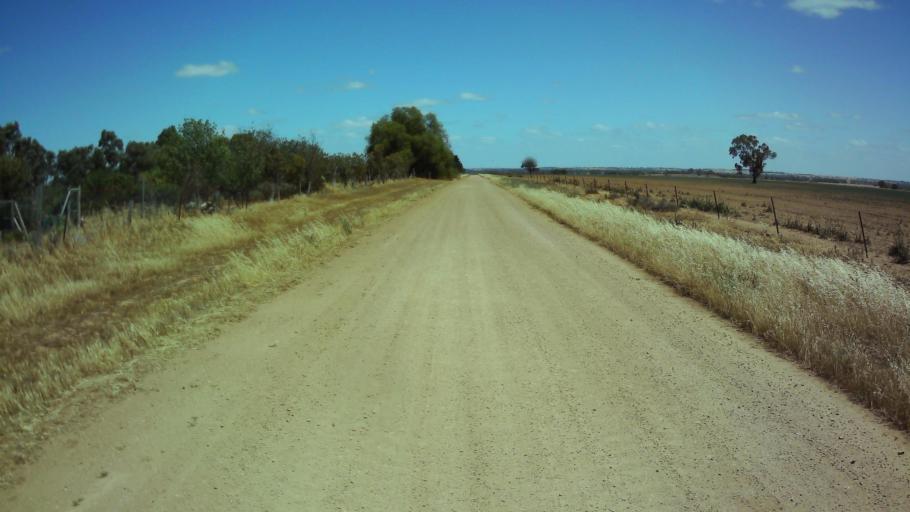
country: AU
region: New South Wales
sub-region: Weddin
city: Grenfell
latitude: -33.9718
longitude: 148.3279
